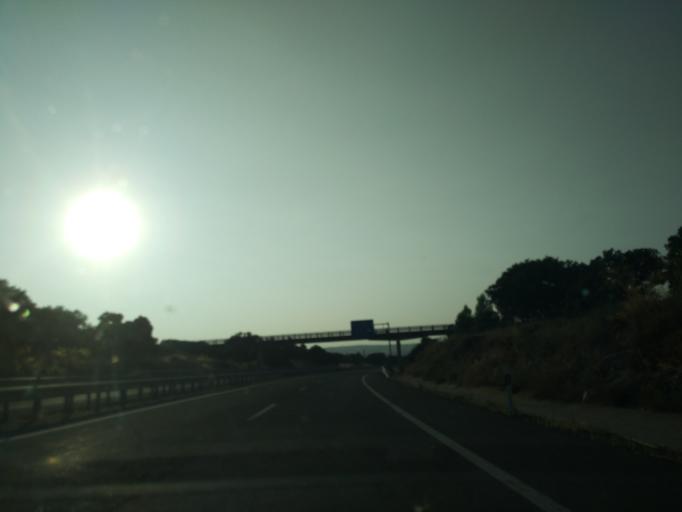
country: ES
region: Castille and Leon
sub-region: Provincia de Avila
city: Avila
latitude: 40.6711
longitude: -4.6747
